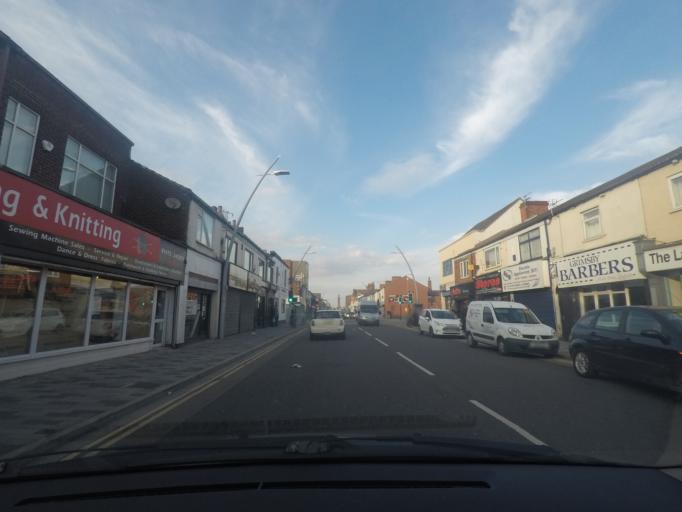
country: GB
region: England
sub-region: North East Lincolnshire
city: Grimsby
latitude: 53.5684
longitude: -0.0745
